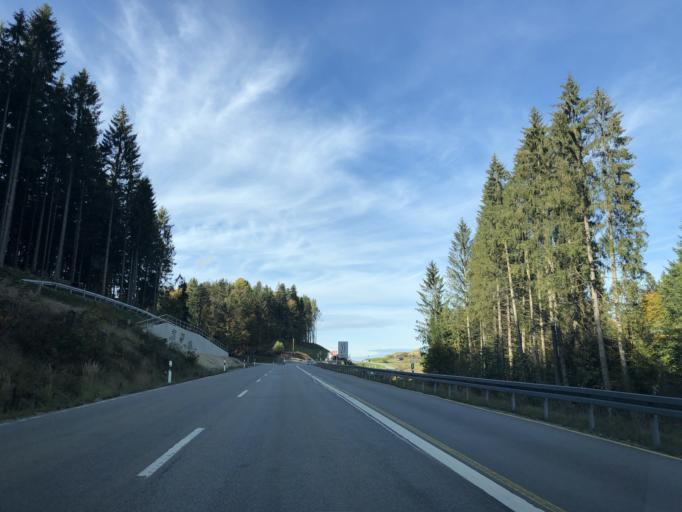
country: DE
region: Bavaria
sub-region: Lower Bavaria
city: Gotteszell
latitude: 48.9429
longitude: 12.9781
